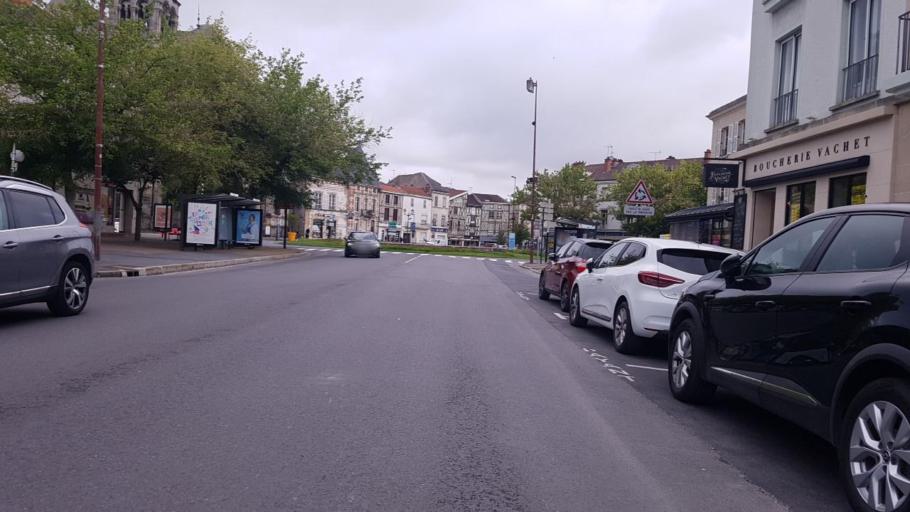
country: FR
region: Champagne-Ardenne
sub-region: Departement de la Marne
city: Chalons-en-Champagne
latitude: 48.9568
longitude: 4.3650
